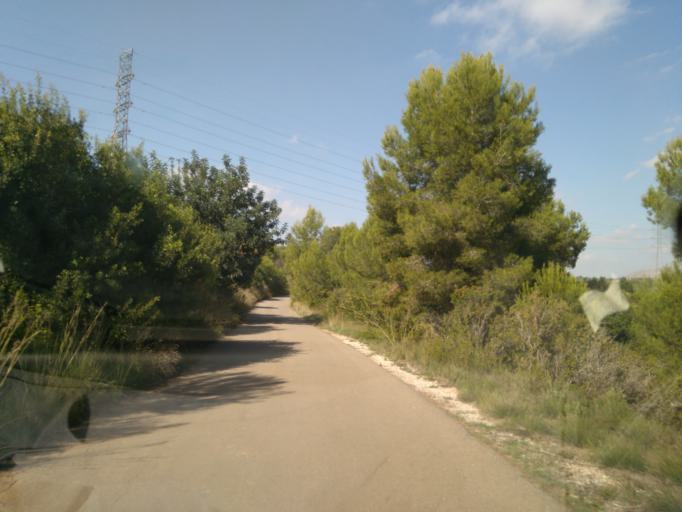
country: ES
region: Valencia
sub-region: Provincia de Valencia
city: Tous
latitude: 39.1754
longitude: -0.5953
